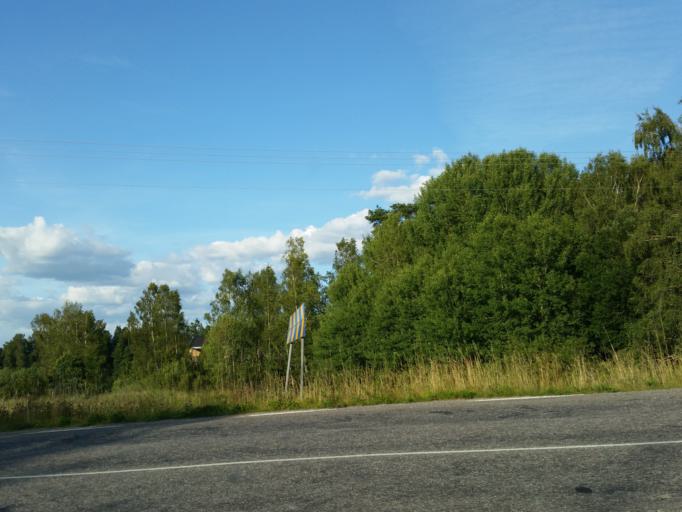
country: SE
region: Stockholm
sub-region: Sodertalje Kommun
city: Molnbo
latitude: 58.9928
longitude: 17.4166
